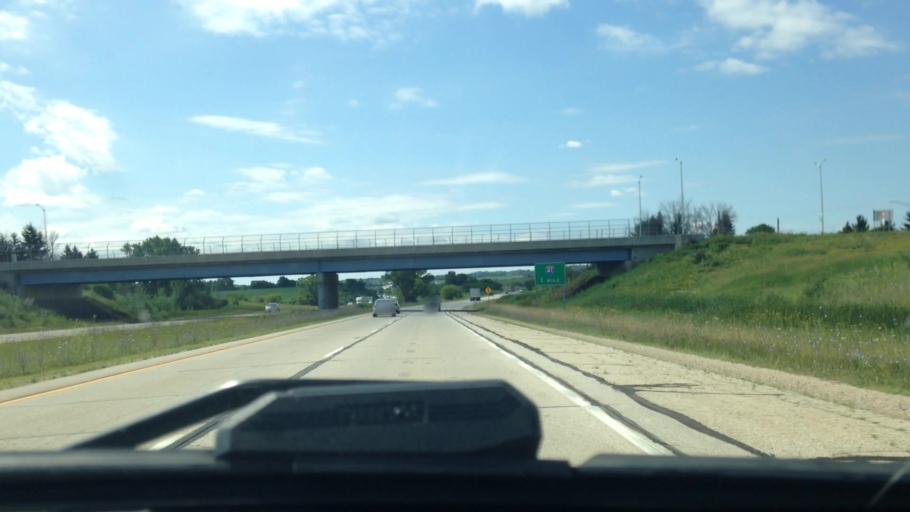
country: US
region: Wisconsin
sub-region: Washington County
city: Richfield
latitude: 43.2850
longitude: -88.1863
